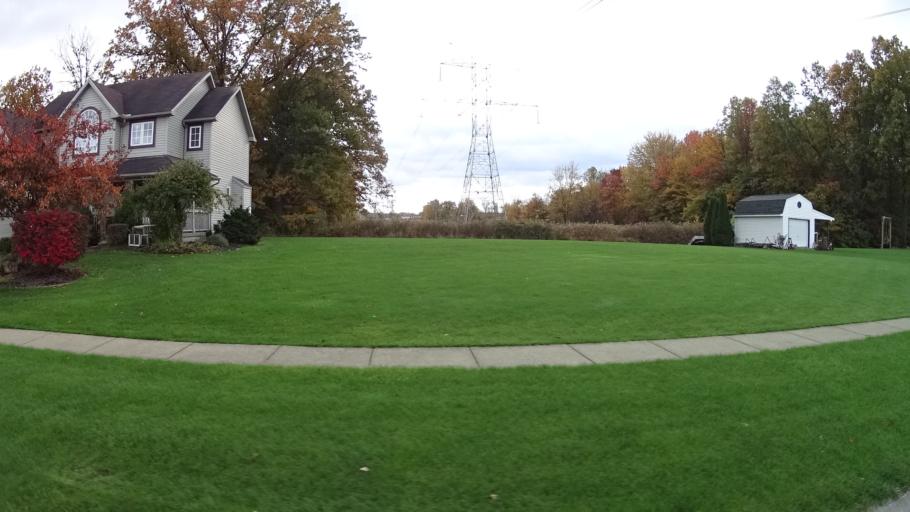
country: US
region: Ohio
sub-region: Lorain County
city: Amherst
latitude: 41.4227
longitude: -82.2043
